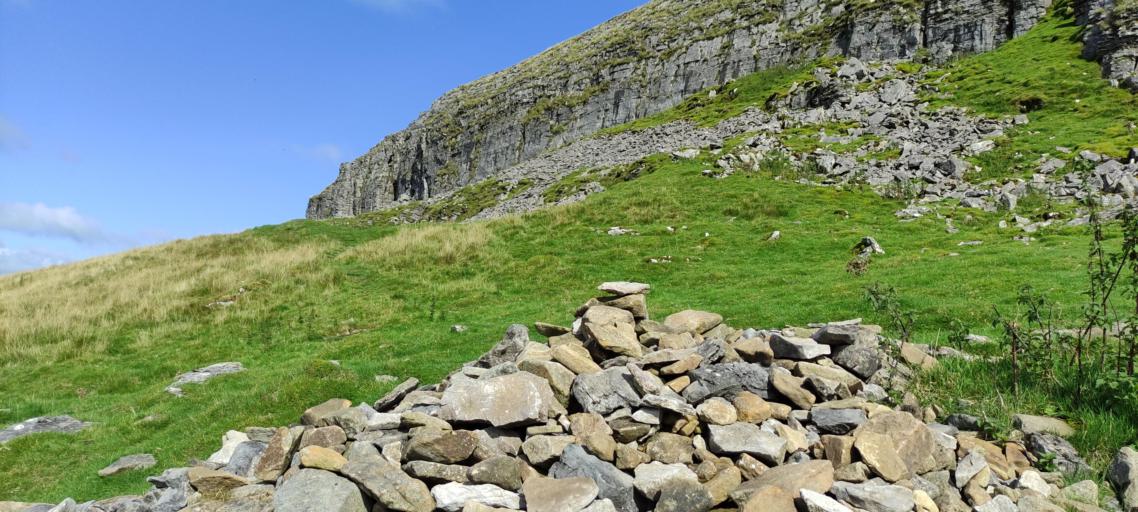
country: GB
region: England
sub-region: North Yorkshire
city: Settle
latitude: 54.1635
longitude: -2.2506
